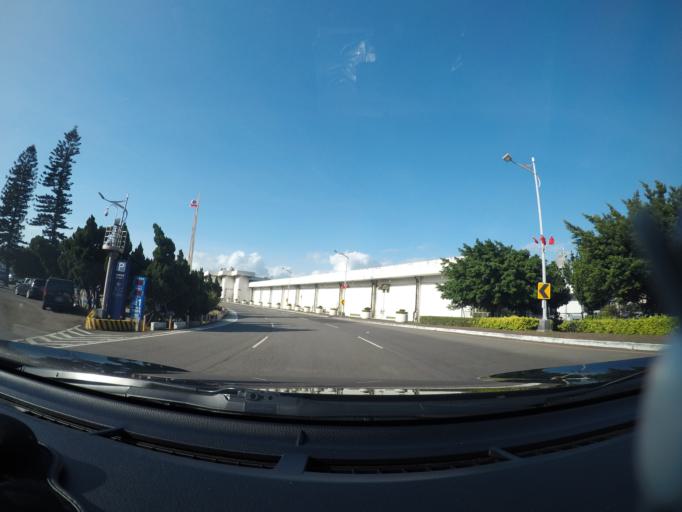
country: TW
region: Taiwan
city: Taoyuan City
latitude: 25.0827
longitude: 121.2402
